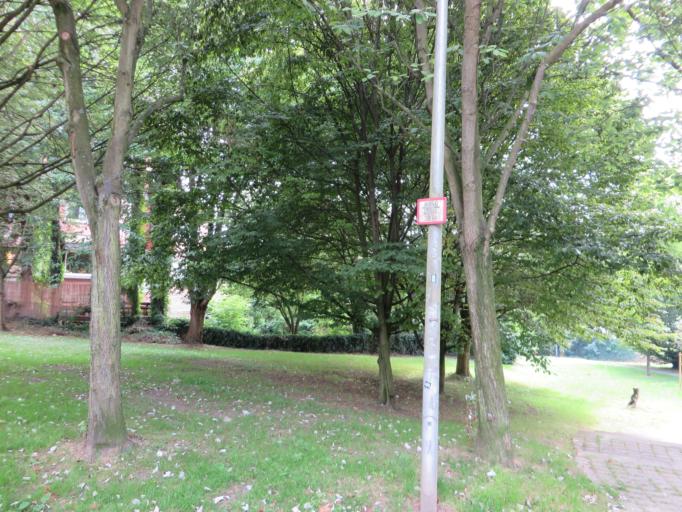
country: DE
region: North Rhine-Westphalia
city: Witten
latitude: 51.4380
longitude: 7.3425
